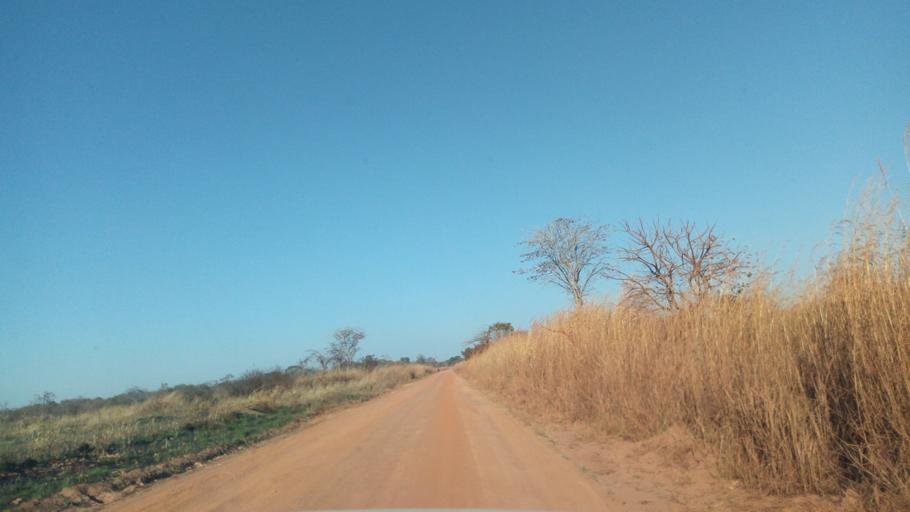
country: ZM
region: Luapula
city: Mwense
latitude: -10.5126
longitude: 28.4659
